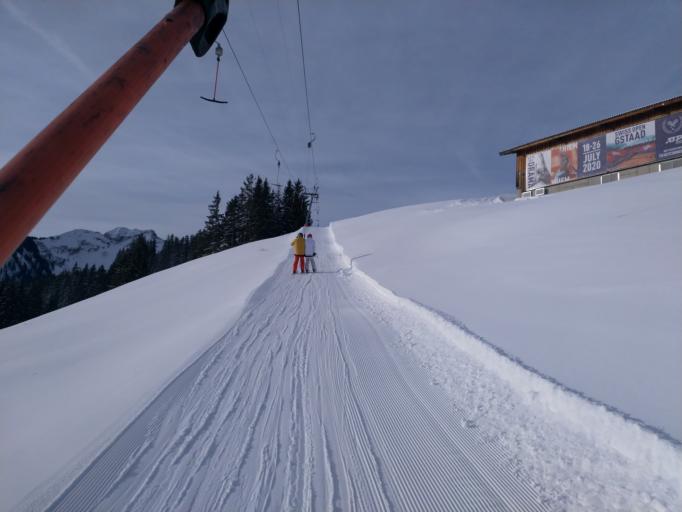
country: CH
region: Bern
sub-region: Obersimmental-Saanen District
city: Gstaad
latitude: 46.4611
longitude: 7.2626
